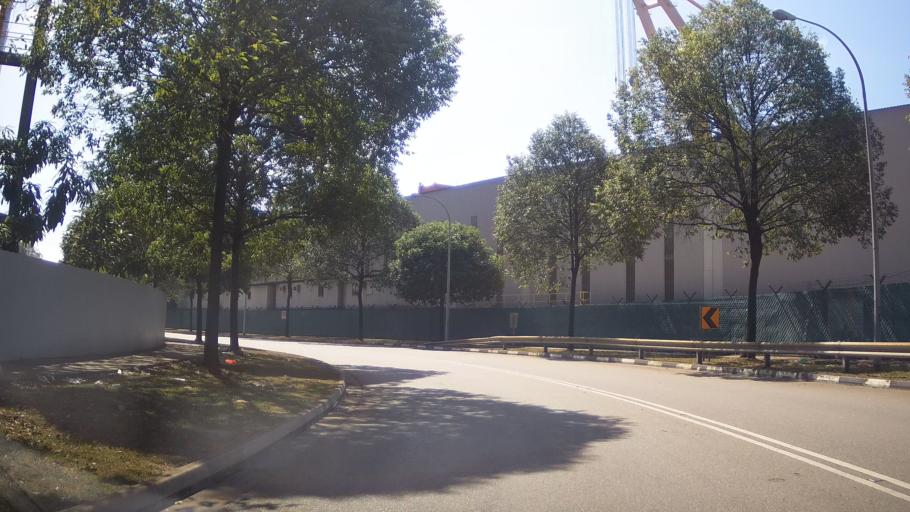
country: SG
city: Singapore
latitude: 1.3012
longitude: 103.6850
